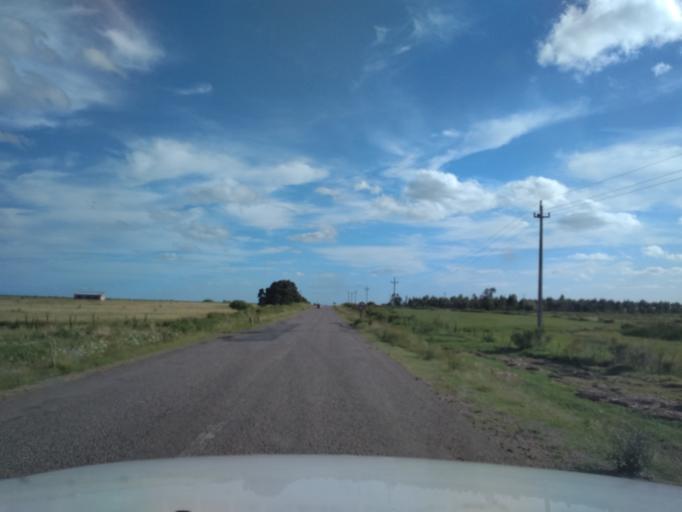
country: UY
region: Canelones
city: San Ramon
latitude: -34.2562
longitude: -55.9267
